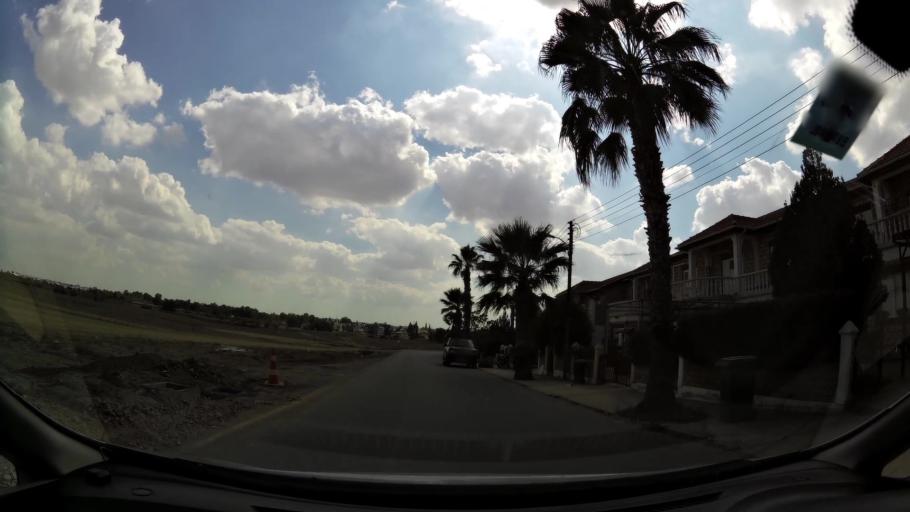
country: CY
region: Lefkosia
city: Nicosia
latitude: 35.2234
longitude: 33.3050
